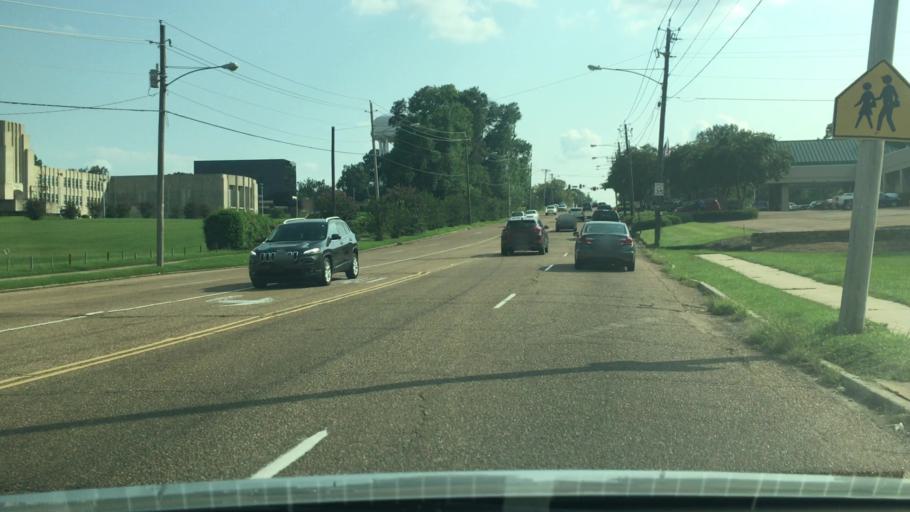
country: US
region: Mississippi
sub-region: Hinds County
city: Jackson
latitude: 32.3262
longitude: -90.1759
